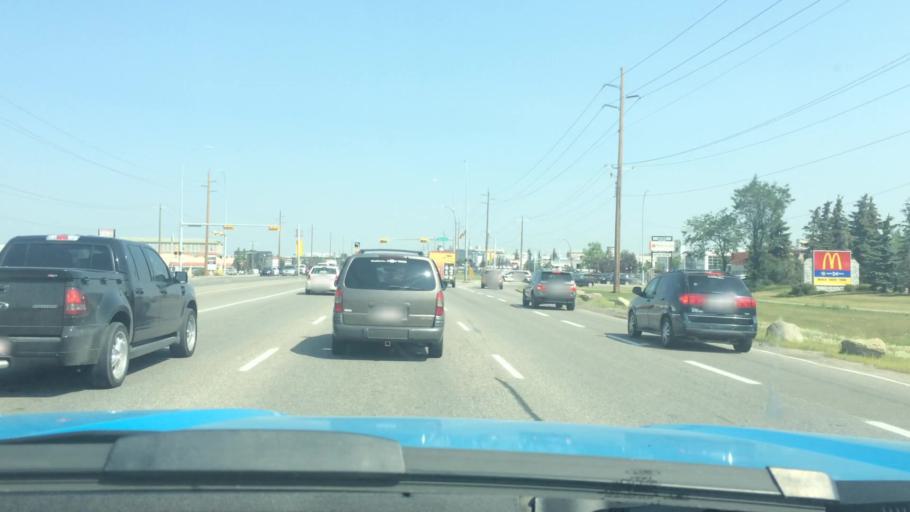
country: CA
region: Alberta
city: Calgary
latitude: 51.0724
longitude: -114.0016
